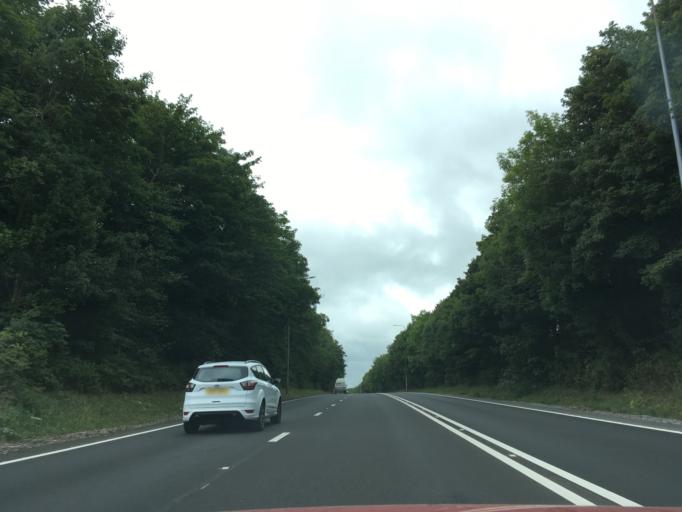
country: GB
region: Wales
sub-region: Carmarthenshire
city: Saint Clears
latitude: 51.8187
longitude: -4.5114
